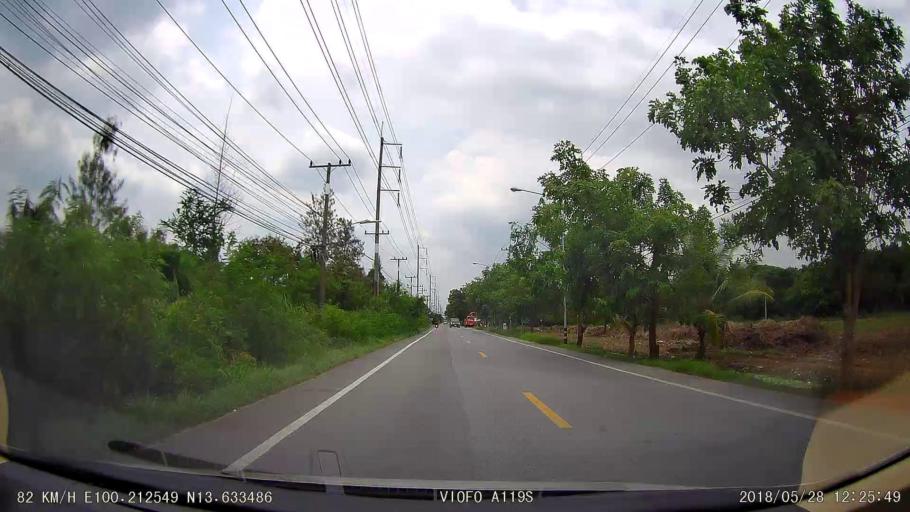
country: TH
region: Samut Sakhon
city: Krathum Baen
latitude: 13.6379
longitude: 100.2260
